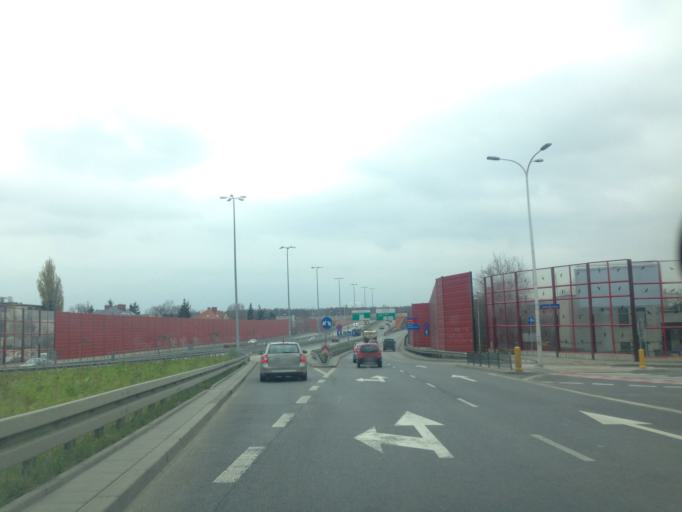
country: PL
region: Masovian Voivodeship
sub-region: Warszawa
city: Rembertow
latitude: 52.2378
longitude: 21.1308
